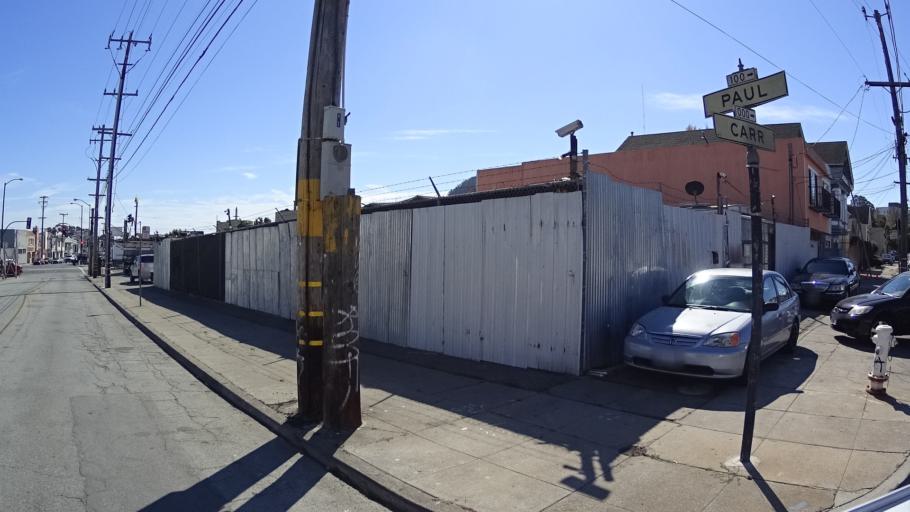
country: US
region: California
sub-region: San Mateo County
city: Brisbane
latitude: 37.7226
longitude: -122.3966
